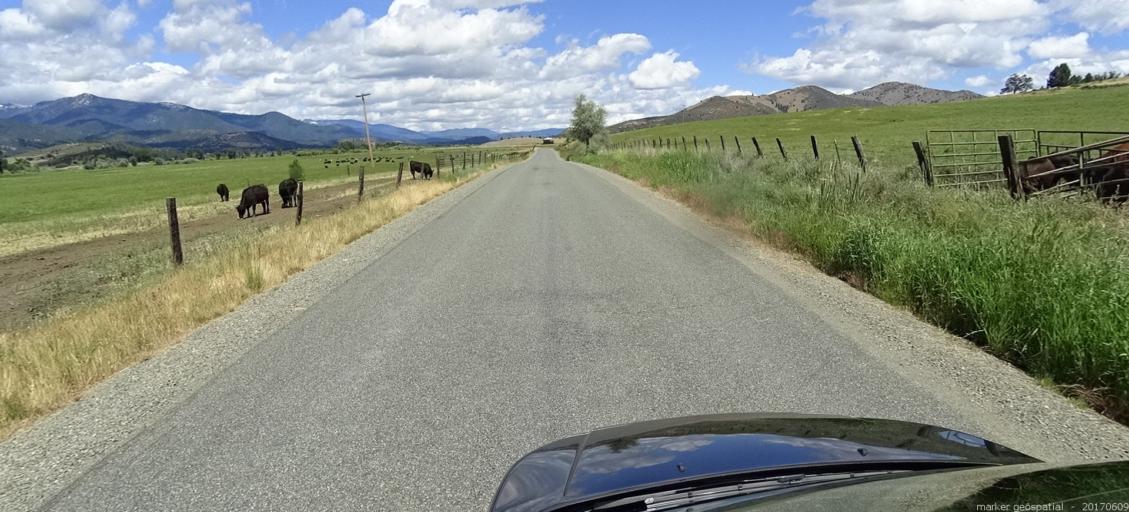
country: US
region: California
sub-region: Siskiyou County
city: Yreka
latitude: 41.3919
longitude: -122.8236
